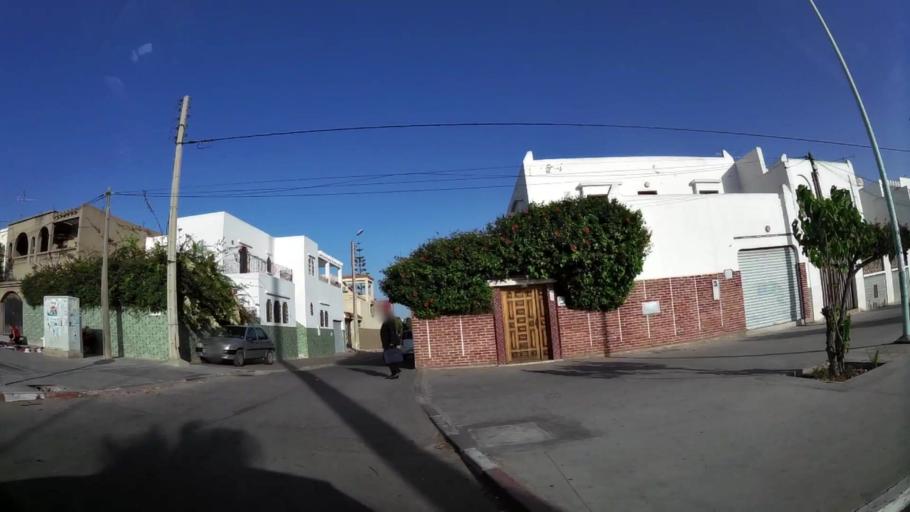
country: MA
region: Oued ed Dahab-Lagouira
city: Dakhla
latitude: 30.4076
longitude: -9.5500
